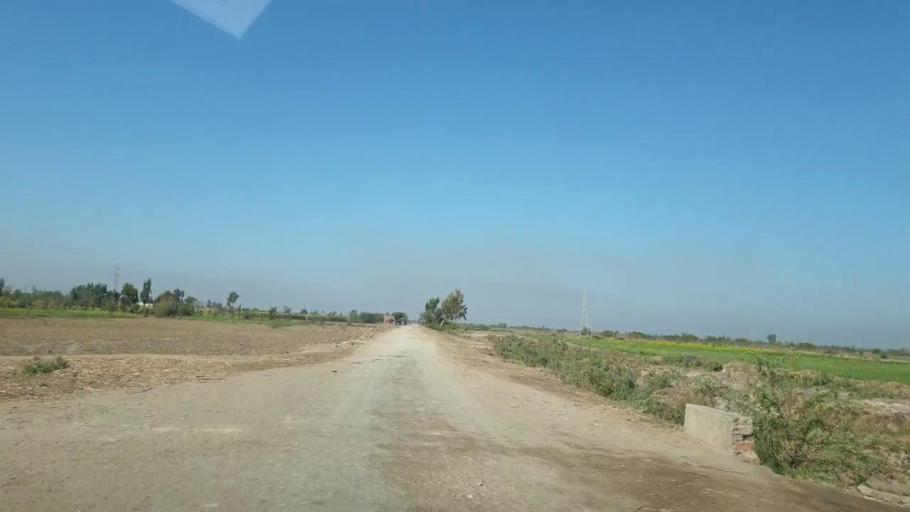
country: PK
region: Sindh
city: Mirpur Khas
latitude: 25.6044
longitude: 69.0322
